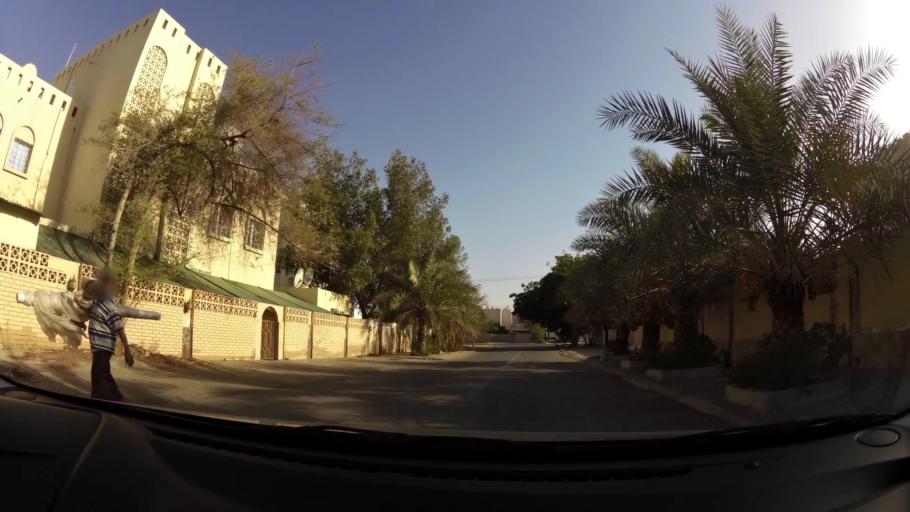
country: OM
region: Muhafazat Masqat
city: As Sib al Jadidah
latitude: 23.6378
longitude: 58.2036
